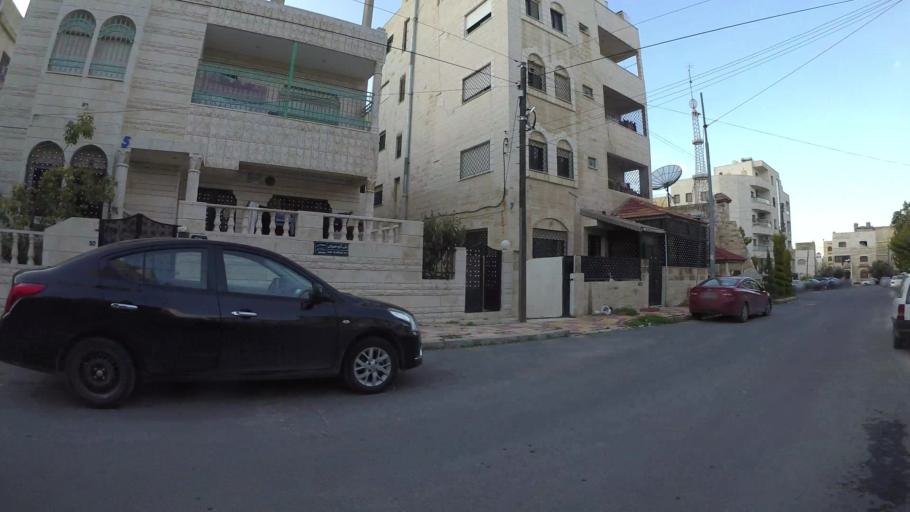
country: JO
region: Amman
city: Al Bunayyat ash Shamaliyah
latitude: 31.9144
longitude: 35.8909
